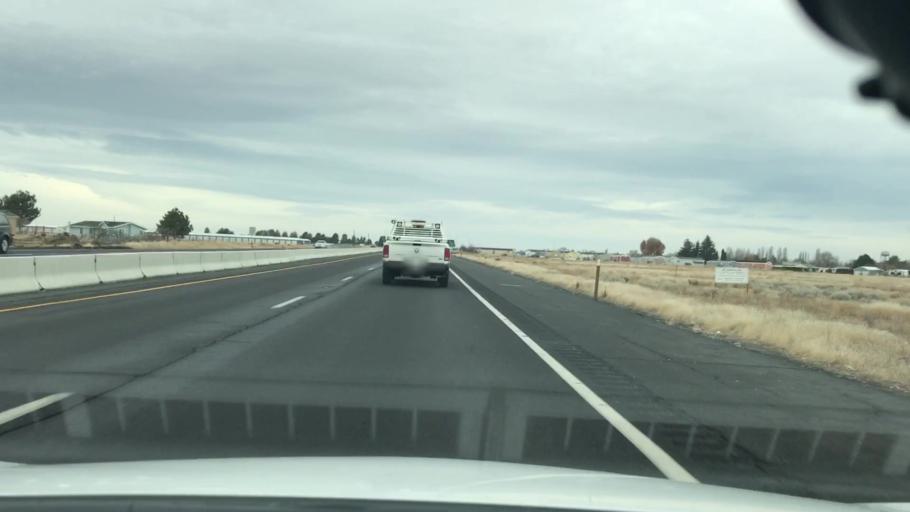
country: US
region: Washington
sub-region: Grant County
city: Cascade Valley
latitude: 47.1537
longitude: -119.3043
